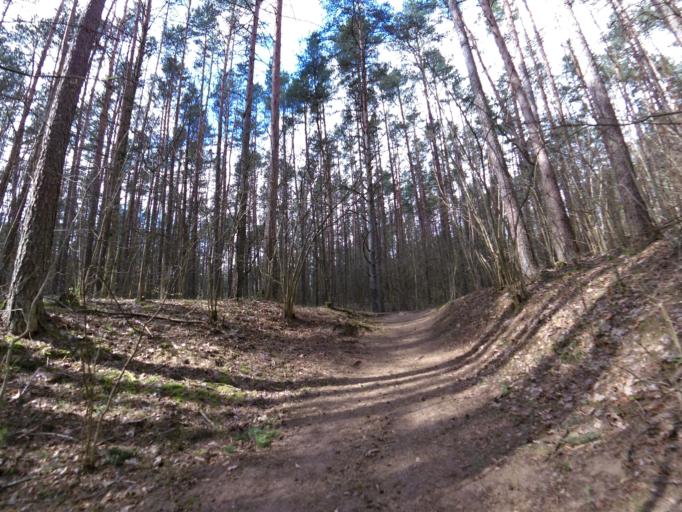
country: LT
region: Vilnius County
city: Pilaite
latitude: 54.6918
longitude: 25.1965
